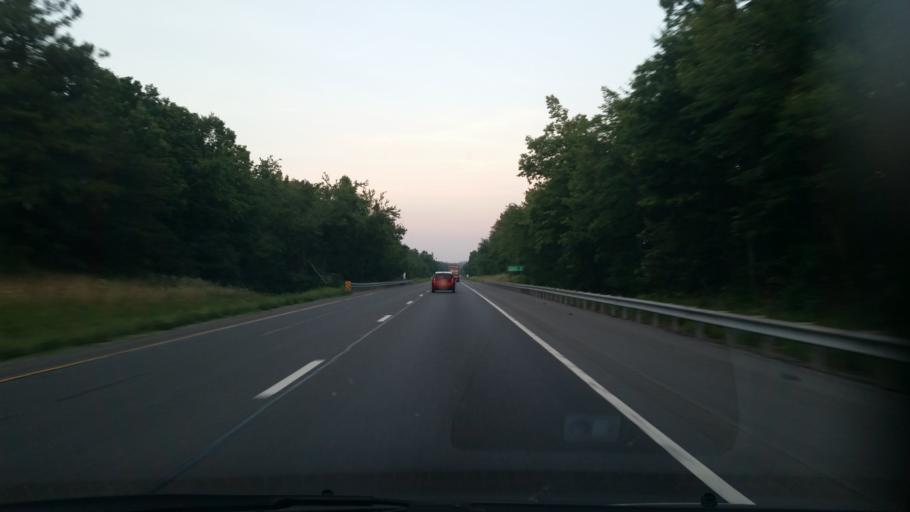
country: US
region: Tennessee
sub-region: Cumberland County
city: Crossville
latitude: 36.0462
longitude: -85.1322
